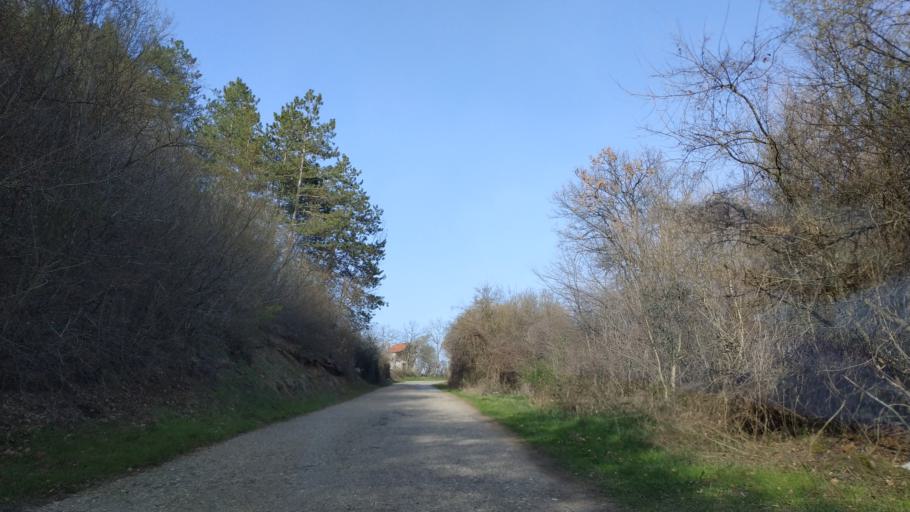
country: RS
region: Central Serbia
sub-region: Nisavski Okrug
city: Aleksinac
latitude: 43.5471
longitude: 21.7204
